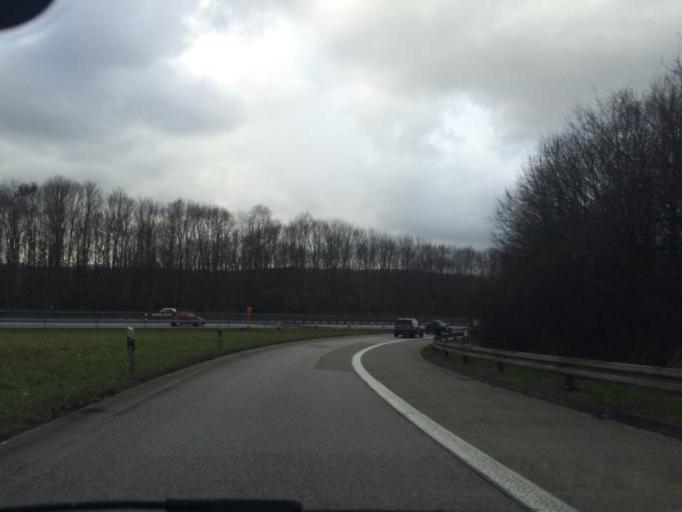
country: DE
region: North Rhine-Westphalia
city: Sprockhovel
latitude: 51.4156
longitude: 7.2638
